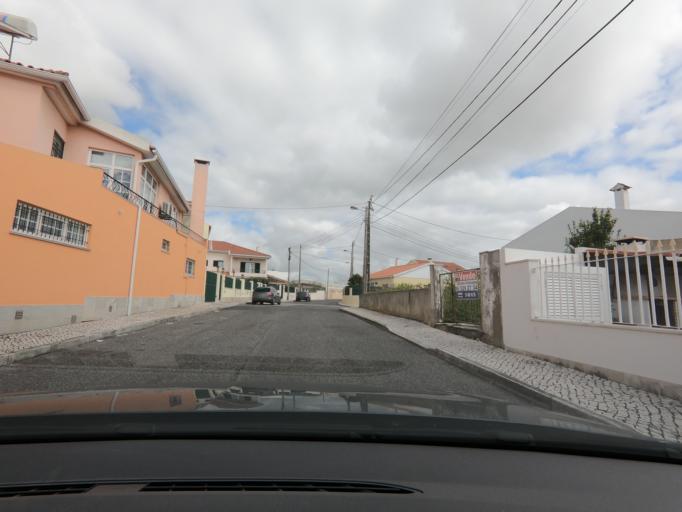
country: PT
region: Lisbon
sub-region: Cascais
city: Sao Domingos de Rana
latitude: 38.7173
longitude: -9.3459
